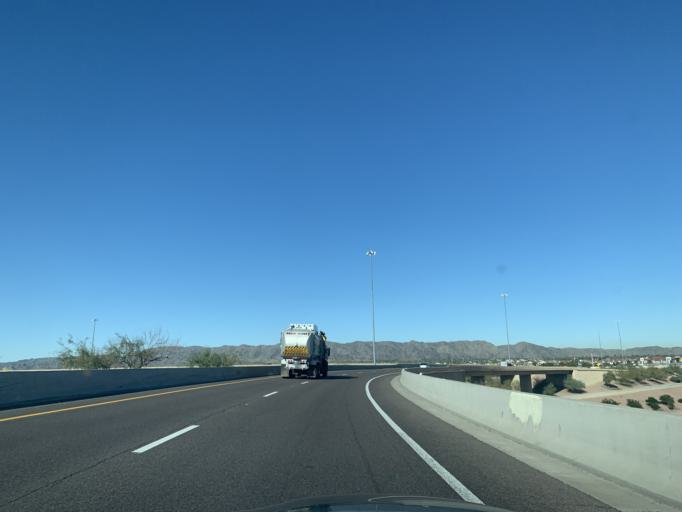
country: US
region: Arizona
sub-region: Maricopa County
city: Guadalupe
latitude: 33.2983
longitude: -111.9701
